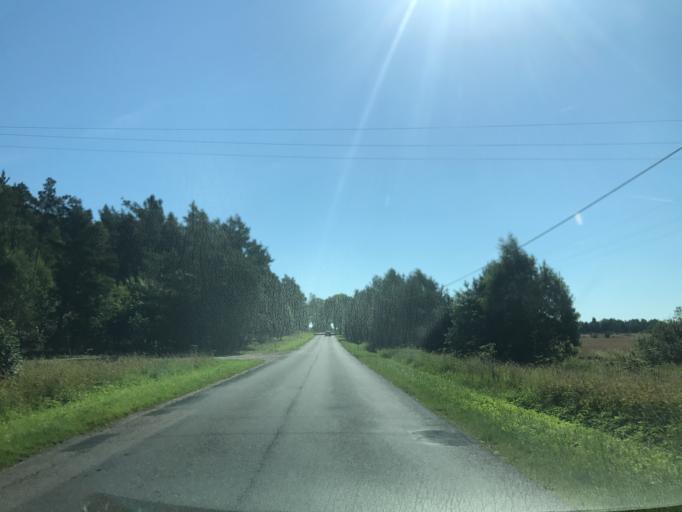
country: PL
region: Pomeranian Voivodeship
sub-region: Powiat bytowski
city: Czarna Dabrowka
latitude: 54.3591
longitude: 17.5448
